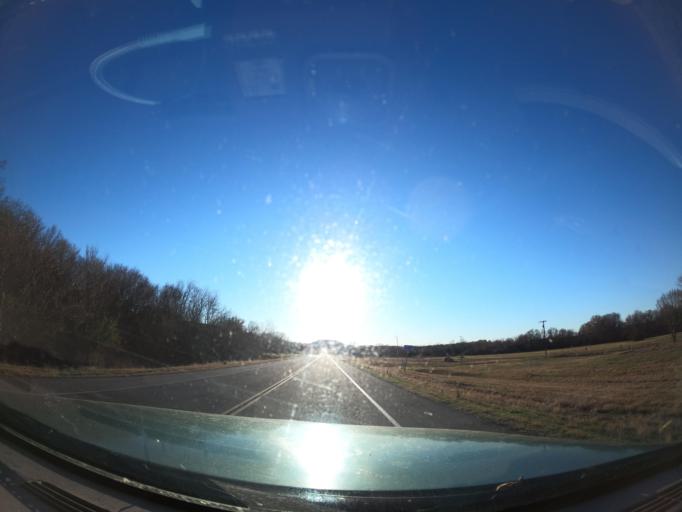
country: US
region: Oklahoma
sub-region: Pittsburg County
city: Hartshorne
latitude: 34.8700
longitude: -95.5172
